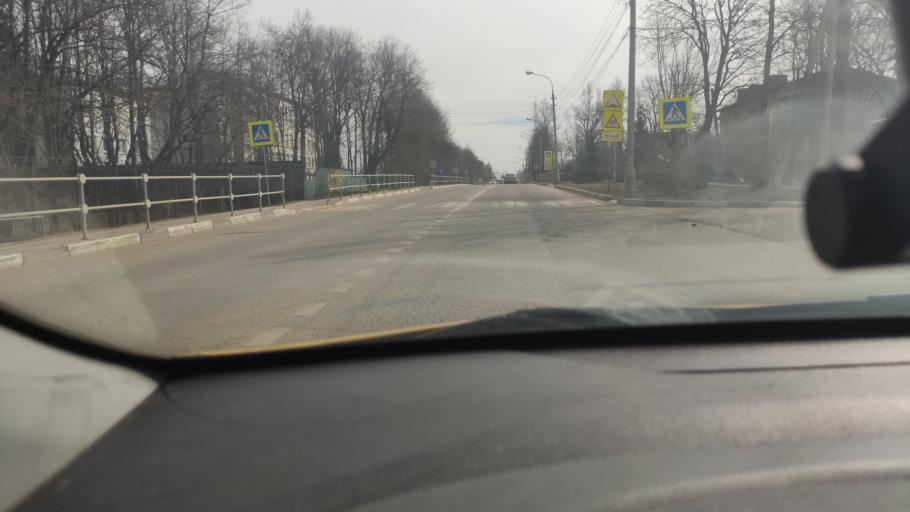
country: RU
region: Moskovskaya
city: Ruza
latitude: 55.7065
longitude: 36.1857
